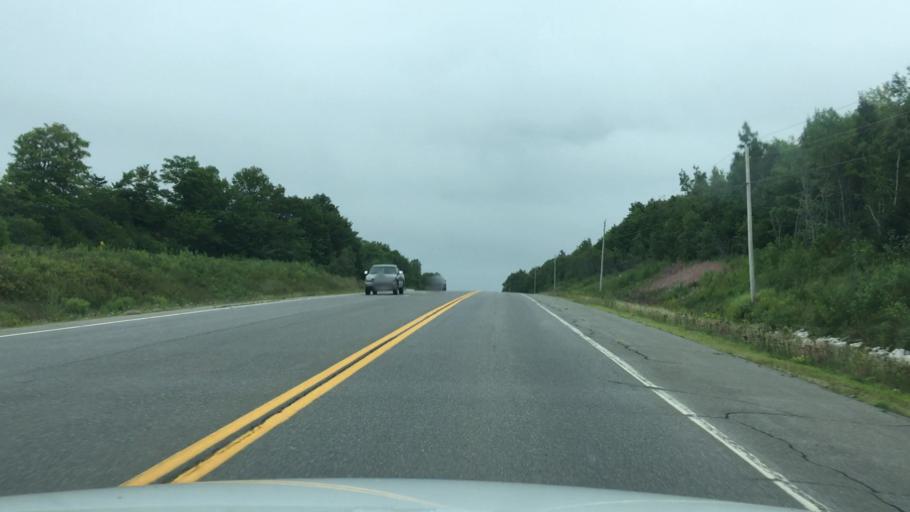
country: US
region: Maine
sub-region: Hancock County
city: Franklin
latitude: 44.8278
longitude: -68.1231
